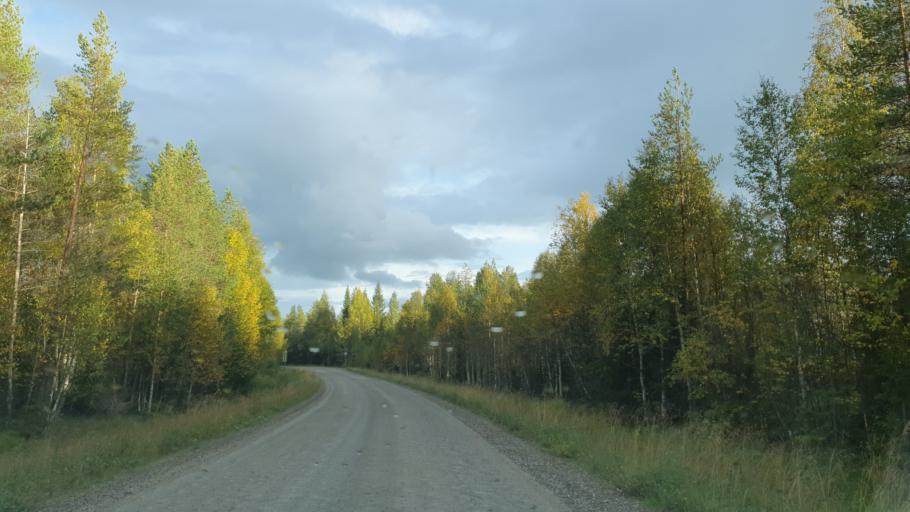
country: FI
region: Kainuu
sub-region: Kehys-Kainuu
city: Kuhmo
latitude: 64.4292
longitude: 29.3248
